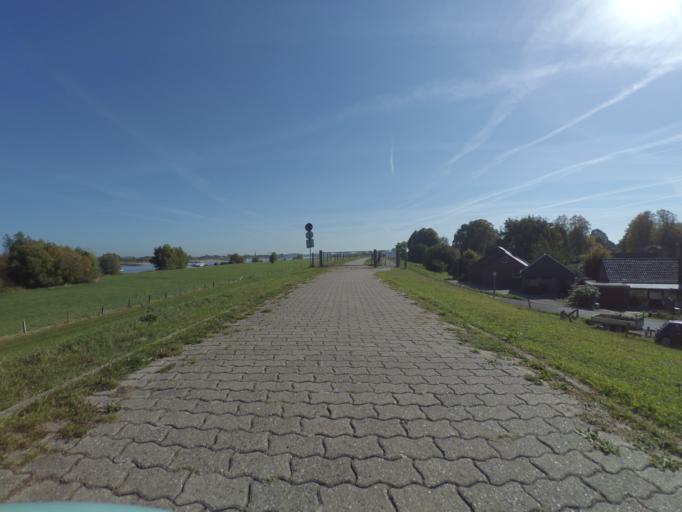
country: NL
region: Gelderland
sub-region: Gemeente Zevenaar
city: Zevenaar
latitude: 51.8601
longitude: 6.0681
